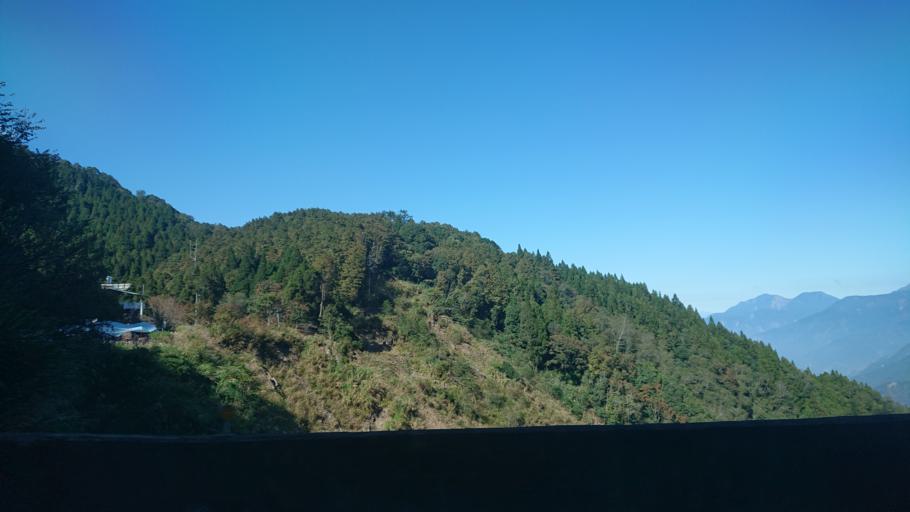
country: TW
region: Taiwan
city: Lugu
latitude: 23.4828
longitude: 120.8308
